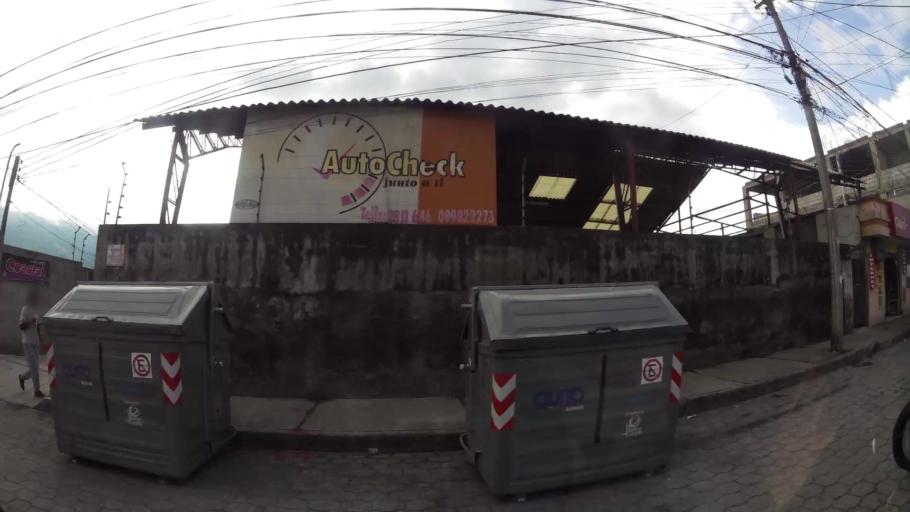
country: EC
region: Pichincha
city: Quito
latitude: -0.1464
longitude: -78.4734
